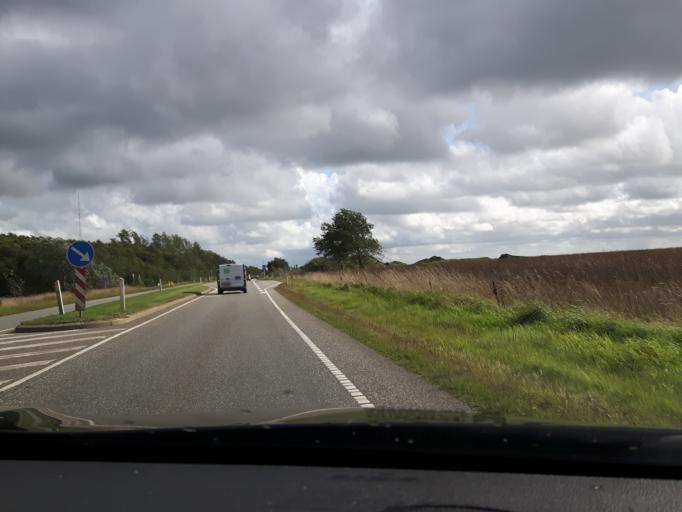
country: DK
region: Central Jutland
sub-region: Herning Kommune
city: Avlum
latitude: 56.2498
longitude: 8.7954
